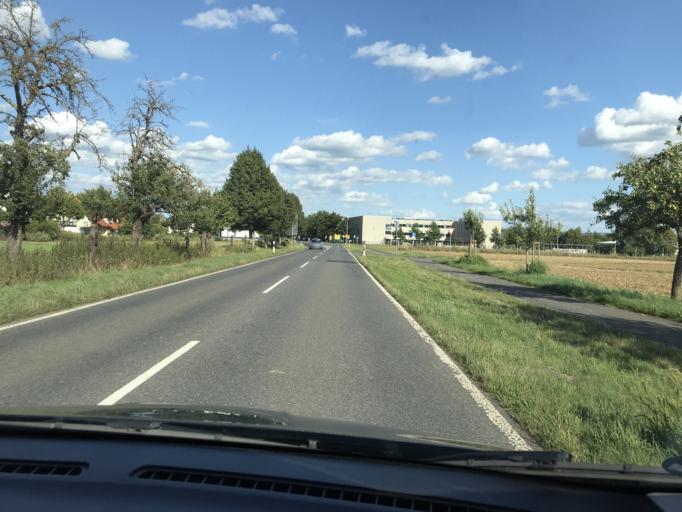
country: DE
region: Bavaria
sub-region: Regierungsbezirk Unterfranken
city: Grossostheim
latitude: 49.9212
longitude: 9.0620
